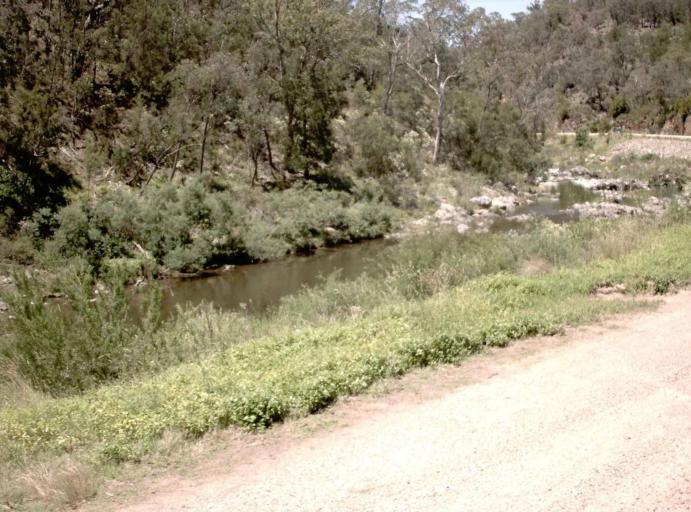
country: AU
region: Victoria
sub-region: East Gippsland
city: Bairnsdale
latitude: -37.4291
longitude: 147.8327
